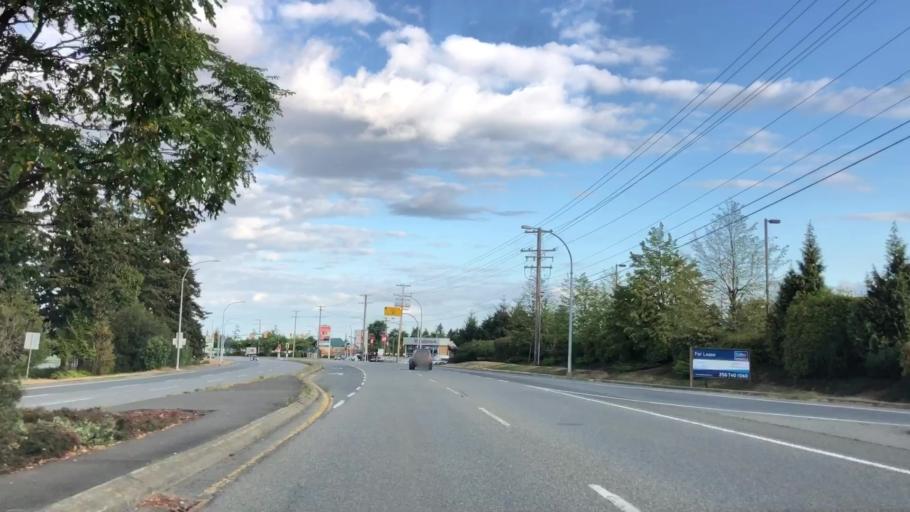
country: CA
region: British Columbia
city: Nanaimo
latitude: 49.2372
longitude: -124.0468
